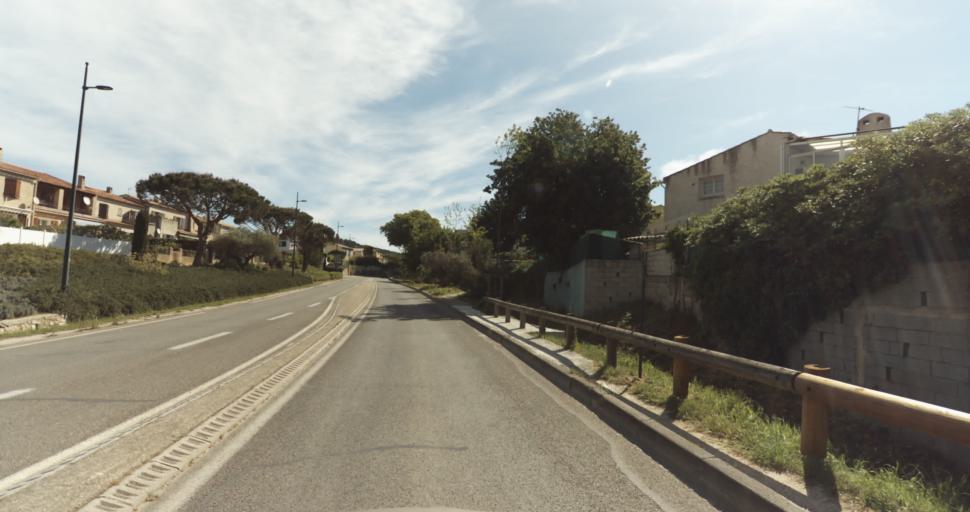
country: FR
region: Provence-Alpes-Cote d'Azur
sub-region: Departement du Var
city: Sanary-sur-Mer
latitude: 43.1071
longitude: 5.8221
